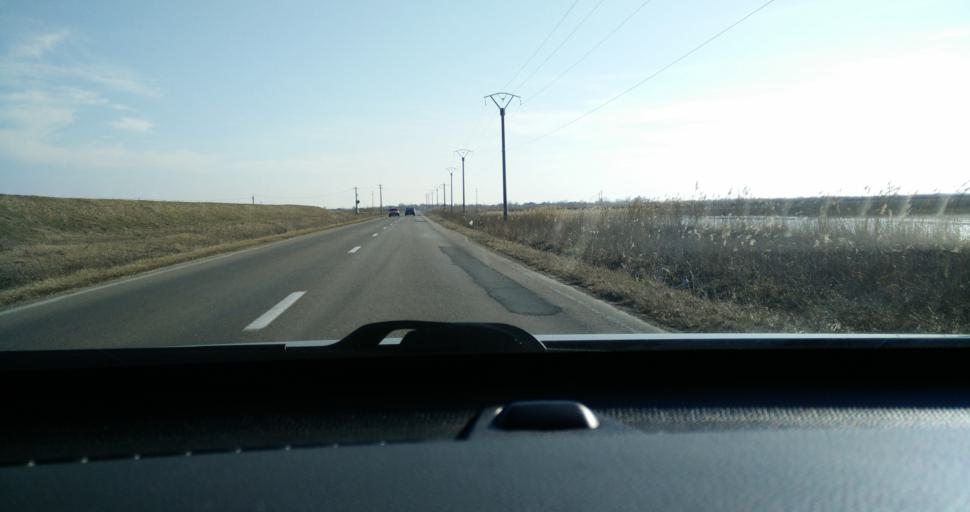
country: RO
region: Vrancea
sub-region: Comuna Nanesti
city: Nanesti
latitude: 45.5626
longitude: 27.4997
